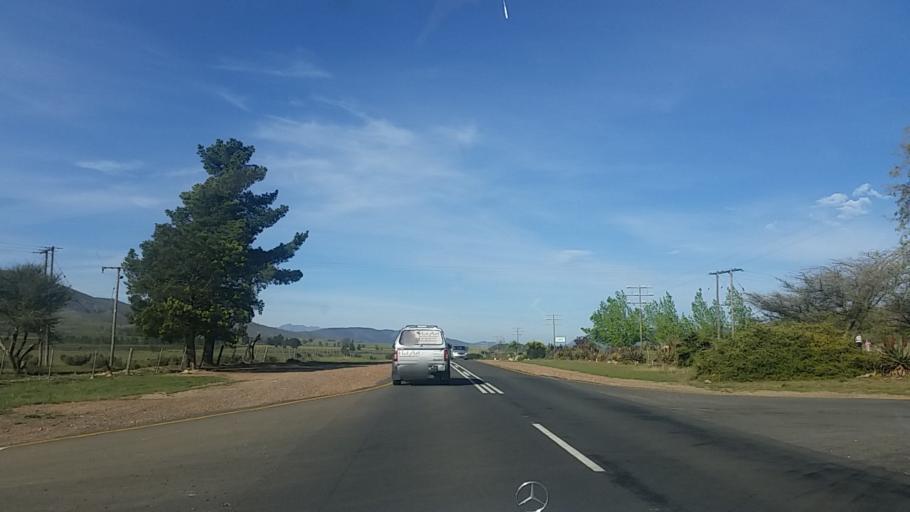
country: ZA
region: Western Cape
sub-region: Eden District Municipality
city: George
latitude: -33.8330
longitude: 22.4536
